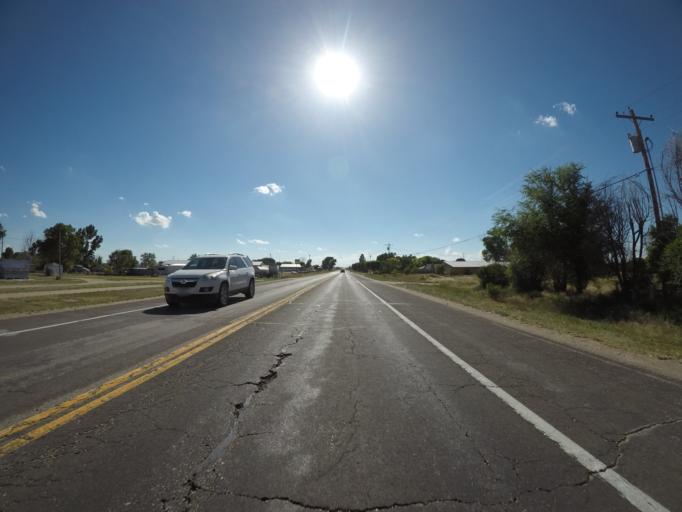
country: US
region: Colorado
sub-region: Logan County
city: Sterling
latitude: 40.6239
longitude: -103.2987
